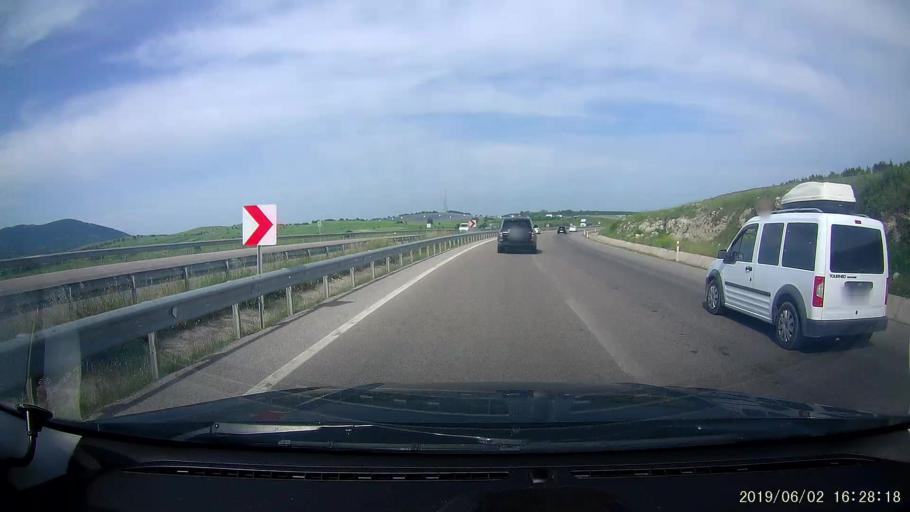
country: TR
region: Samsun
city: Ladik
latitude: 41.0072
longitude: 35.8437
